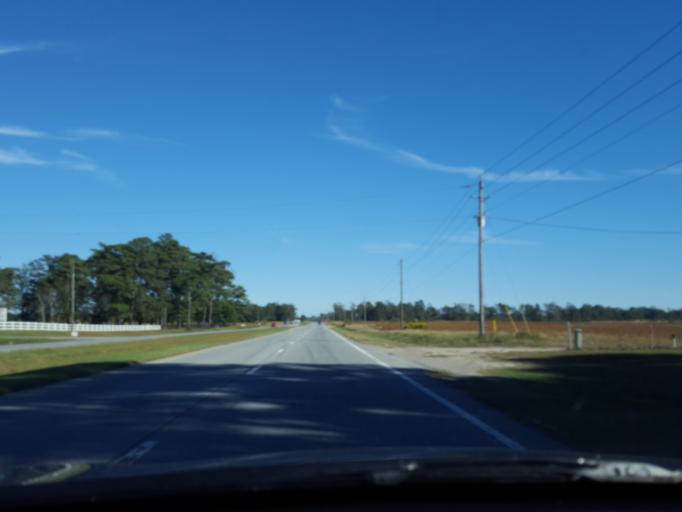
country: US
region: North Carolina
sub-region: Pitt County
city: Greenville
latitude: 35.6234
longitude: -77.2538
